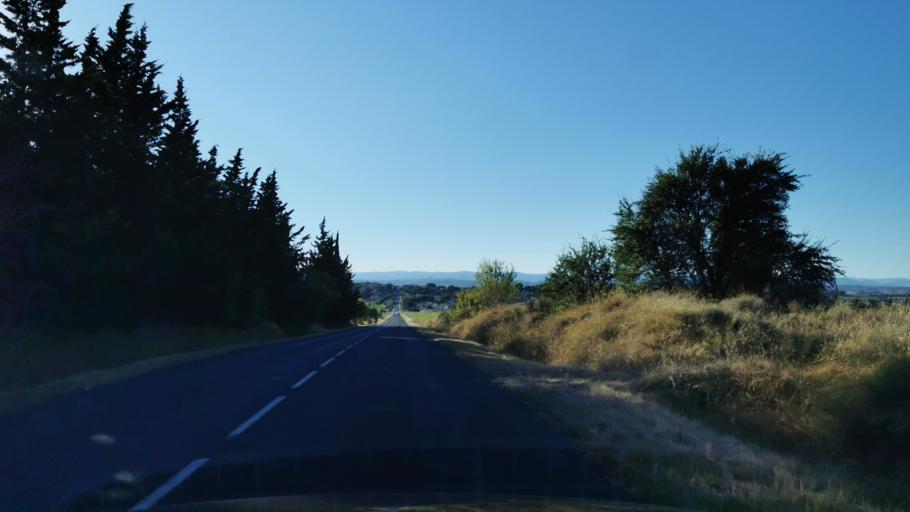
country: FR
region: Languedoc-Roussillon
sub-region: Departement de l'Aude
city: Ouveillan
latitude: 43.2789
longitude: 2.9842
